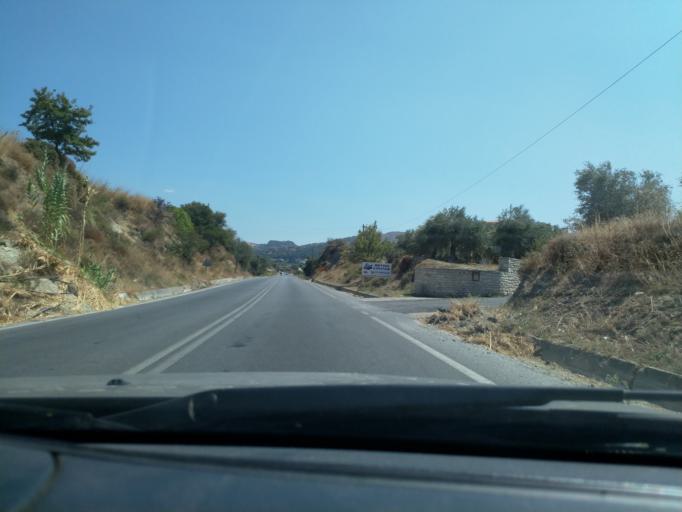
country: GR
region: Crete
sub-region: Nomos Rethymnis
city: Atsipopoulon
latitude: 35.2271
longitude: 24.4768
